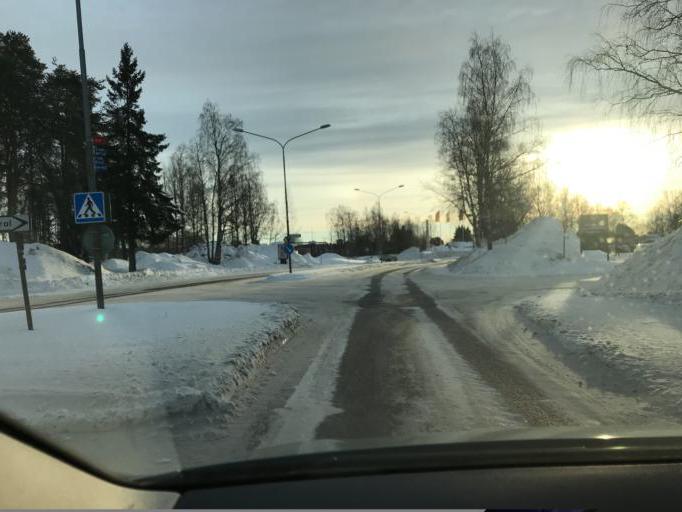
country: SE
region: Norrbotten
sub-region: Lulea Kommun
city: Lulea
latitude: 65.6016
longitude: 22.1299
